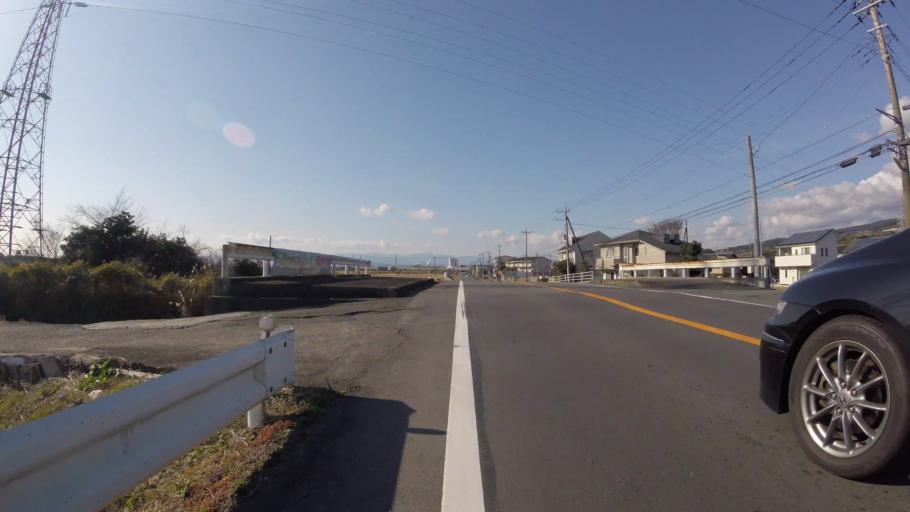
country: JP
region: Shizuoka
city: Fuji
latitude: 35.1534
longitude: 138.7559
